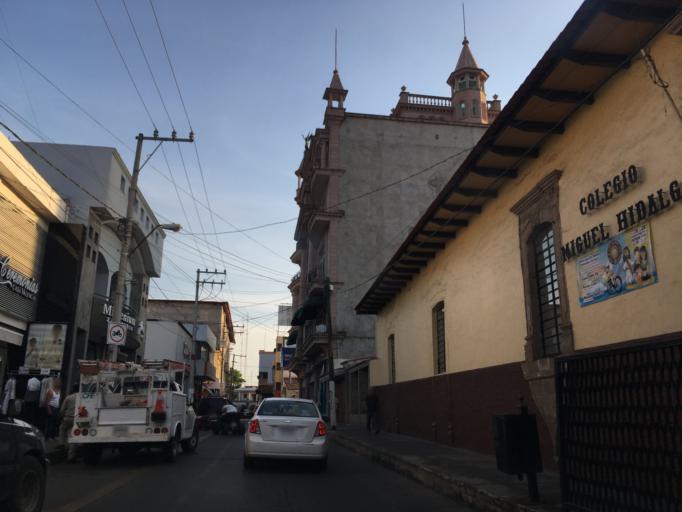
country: MX
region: Michoacan
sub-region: Los Reyes
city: La Higuerita (Colonia San Rafael)
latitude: 19.5910
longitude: -102.4740
